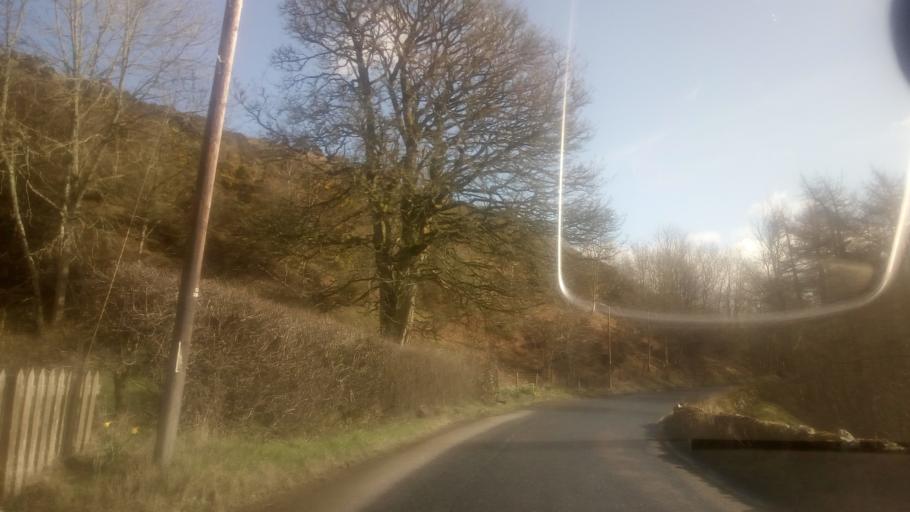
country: GB
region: Scotland
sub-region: The Scottish Borders
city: Hawick
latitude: 55.4161
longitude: -2.8515
